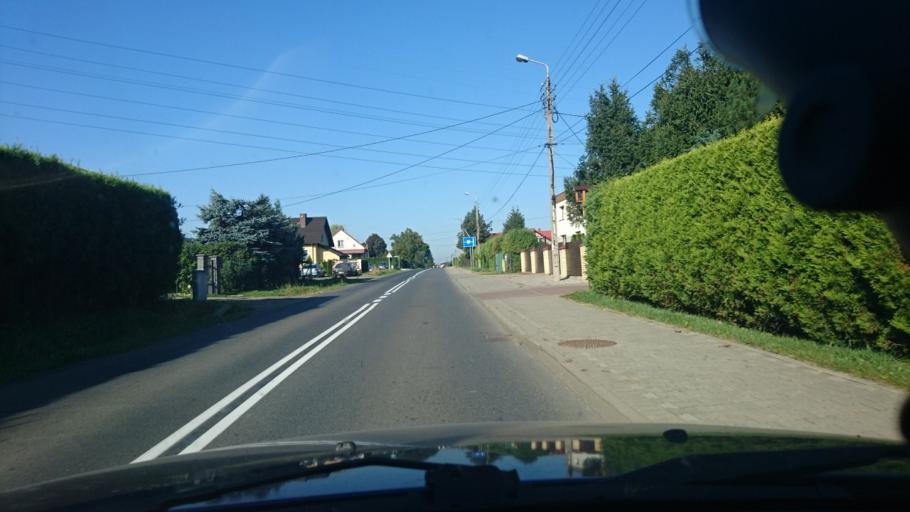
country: PL
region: Silesian Voivodeship
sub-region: Bielsko-Biala
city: Bielsko-Biala
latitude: 49.8507
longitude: 19.0645
